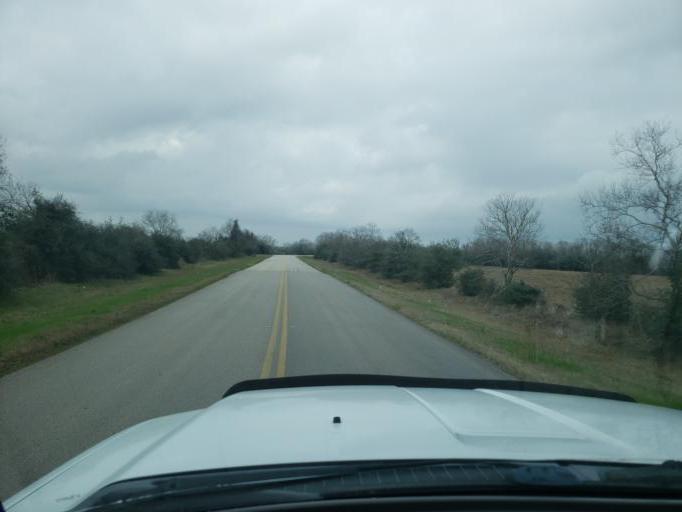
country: US
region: Texas
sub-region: Fort Bend County
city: Needville
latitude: 29.3700
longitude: -95.7295
